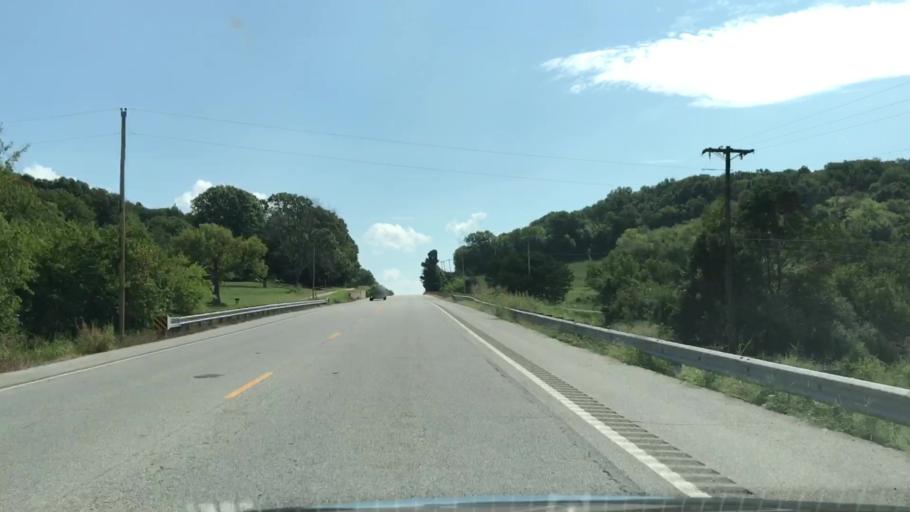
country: US
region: Tennessee
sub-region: Trousdale County
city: Hartsville
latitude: 36.3703
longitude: -86.0990
